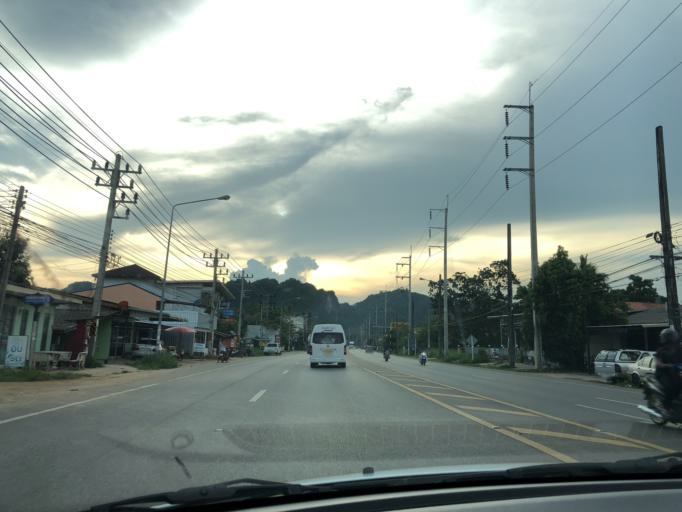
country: TH
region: Krabi
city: Krabi
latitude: 8.0851
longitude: 98.8856
